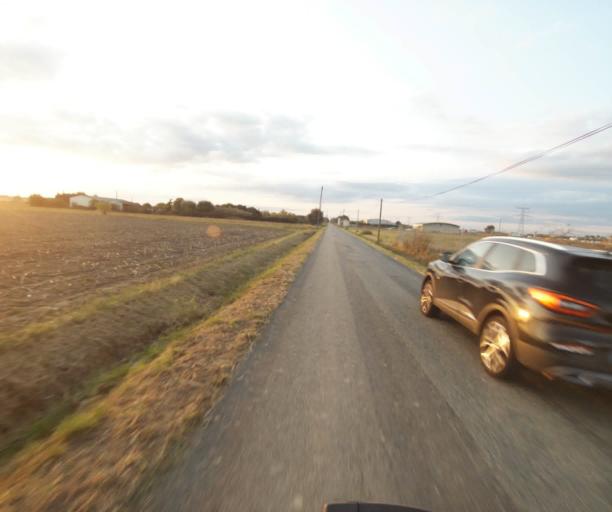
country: FR
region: Midi-Pyrenees
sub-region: Departement du Tarn-et-Garonne
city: Verdun-sur-Garonne
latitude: 43.8209
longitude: 1.2437
